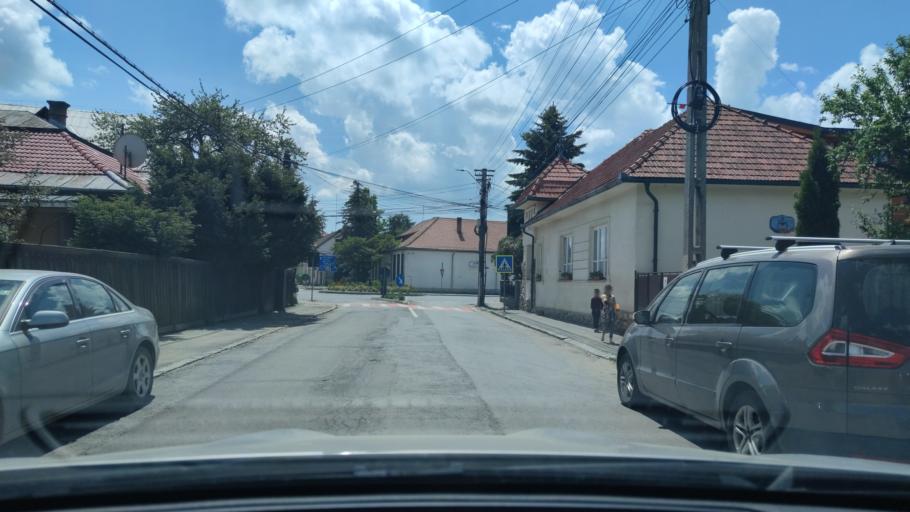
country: RO
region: Harghita
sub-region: Municipiul Gheorgheni
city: Gheorgheni
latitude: 46.7236
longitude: 25.5984
